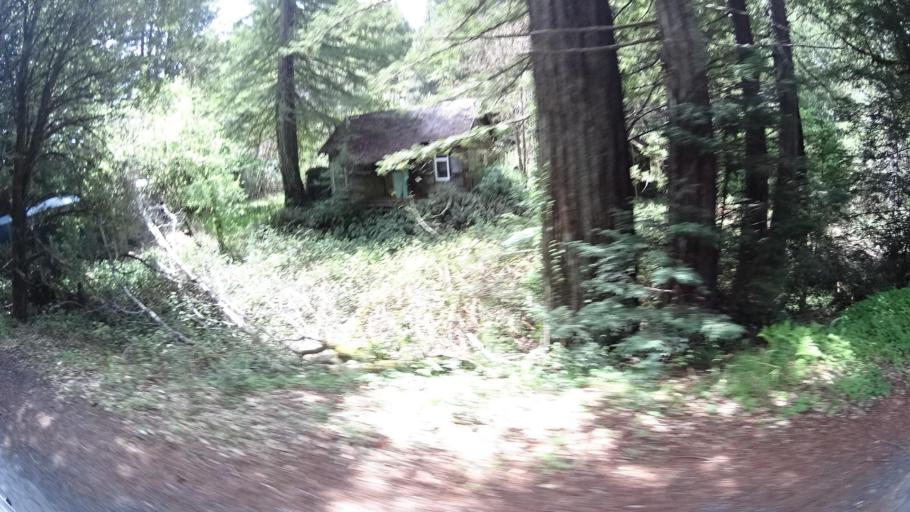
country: US
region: California
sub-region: Humboldt County
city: Redway
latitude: 40.0232
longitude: -123.9417
